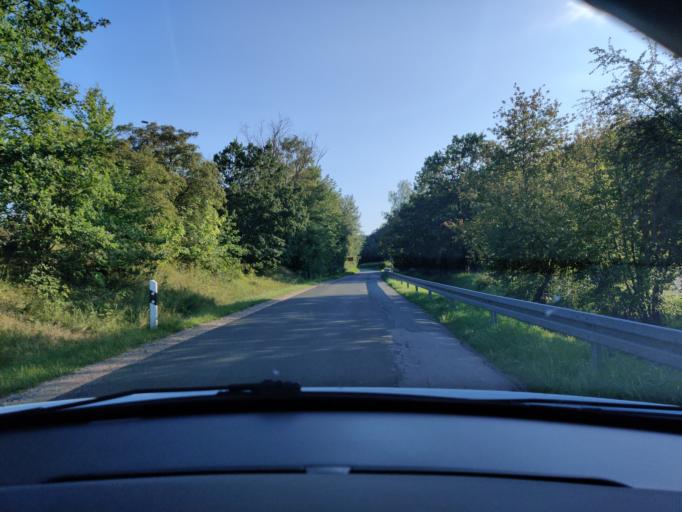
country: DE
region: Bavaria
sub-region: Upper Palatinate
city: Nabburg
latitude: 49.4435
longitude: 12.1762
